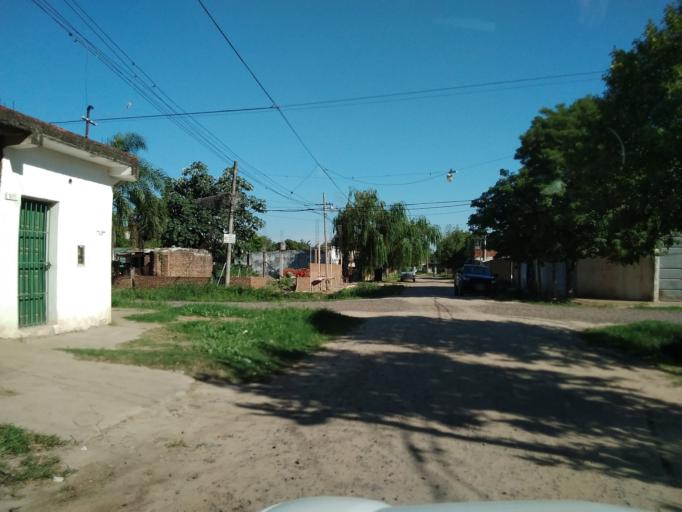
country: AR
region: Corrientes
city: Corrientes
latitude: -27.4808
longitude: -58.8035
